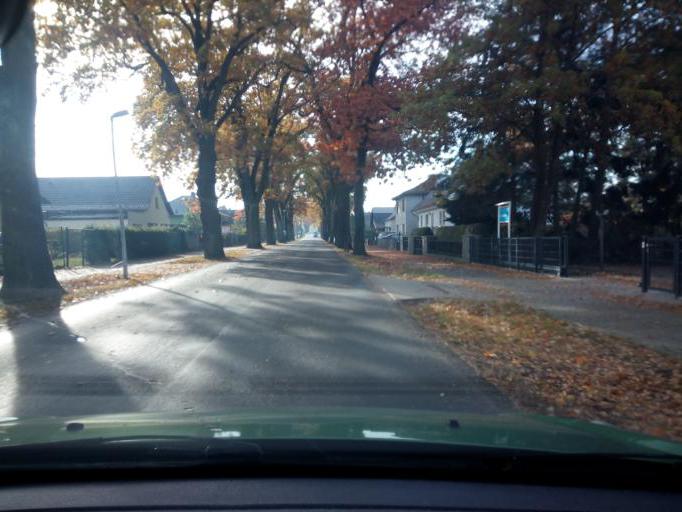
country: DE
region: Brandenburg
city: Neuenhagen
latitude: 52.5122
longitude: 13.7073
